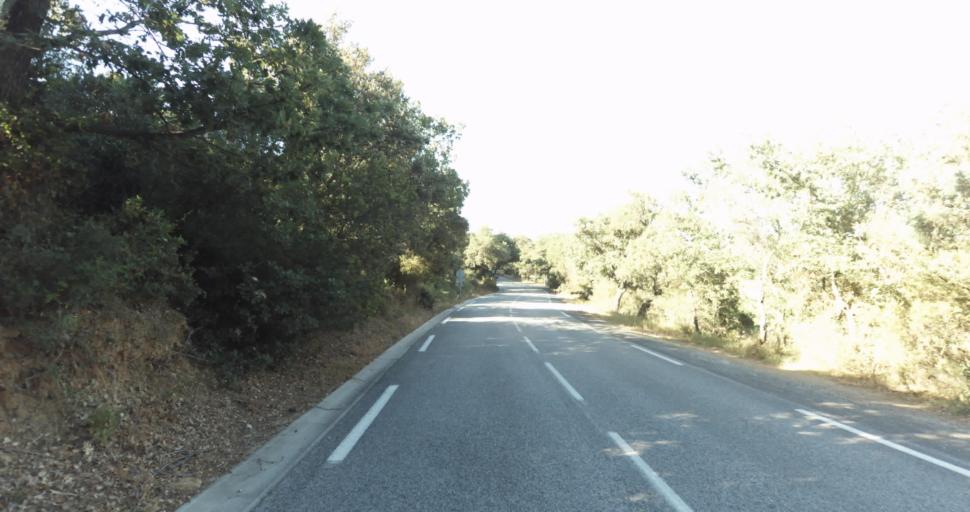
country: FR
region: Provence-Alpes-Cote d'Azur
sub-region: Departement du Var
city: Gassin
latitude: 43.2415
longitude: 6.5878
